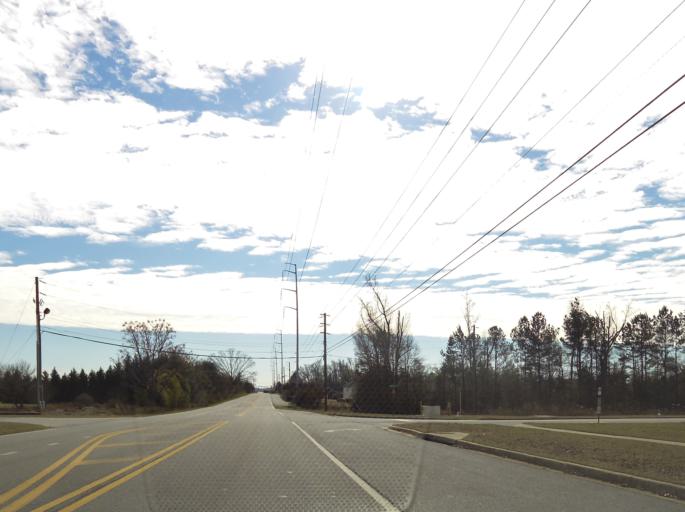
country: US
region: Georgia
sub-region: Bibb County
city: West Point
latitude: 32.8159
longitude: -83.7455
